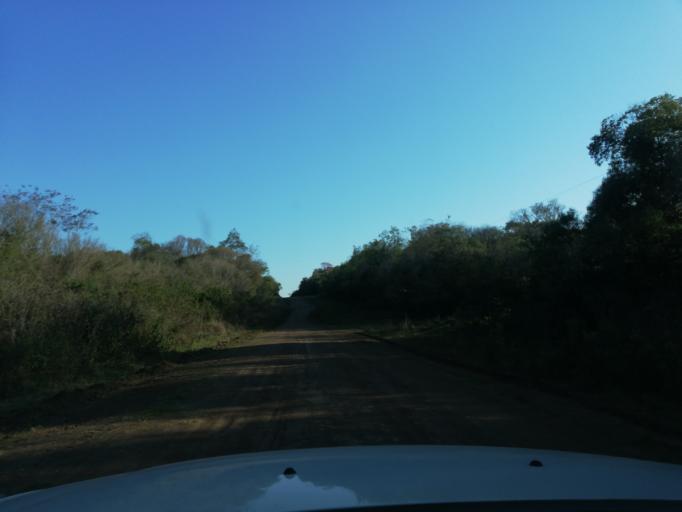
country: AR
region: Misiones
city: Cerro Cora
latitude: -27.5927
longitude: -55.6934
